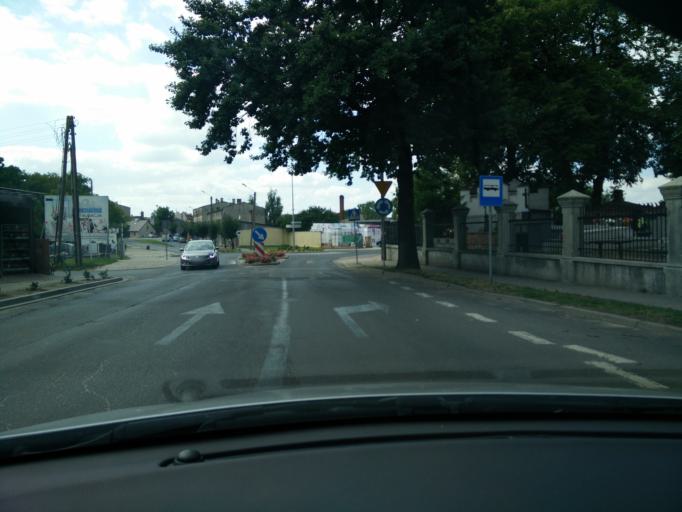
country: PL
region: Greater Poland Voivodeship
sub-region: Powiat sredzki
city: Sroda Wielkopolska
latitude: 52.2317
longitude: 17.2830
